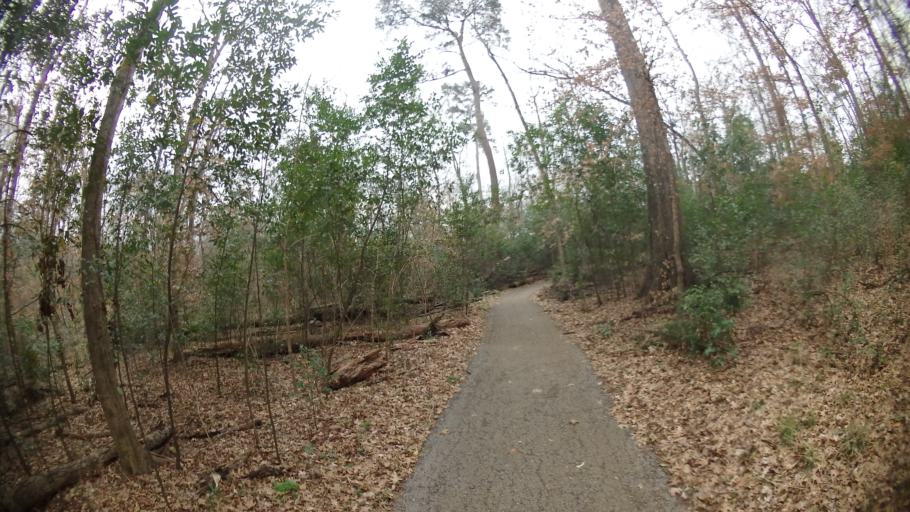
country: US
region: Texas
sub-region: Nacogdoches County
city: Nacogdoches
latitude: 31.6287
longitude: -94.6450
